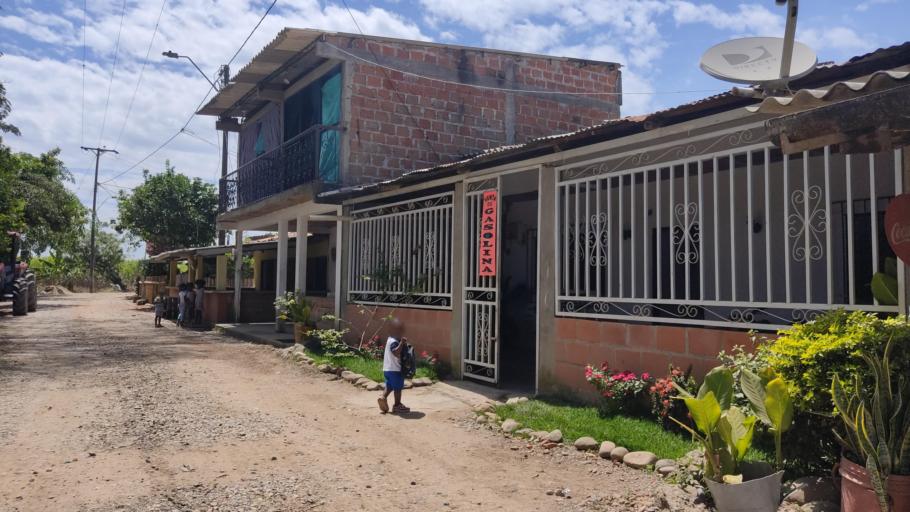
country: CO
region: Valle del Cauca
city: Jamundi
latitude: 3.1618
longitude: -76.5118
